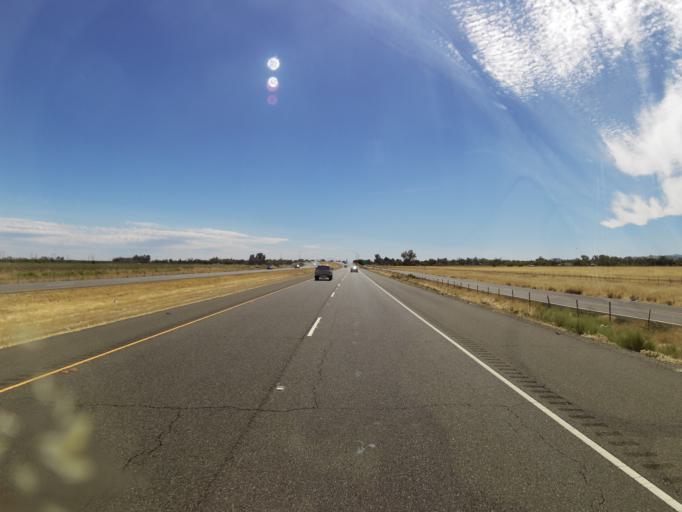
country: US
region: California
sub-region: Solano County
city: Allendale
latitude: 38.4602
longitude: -121.9423
